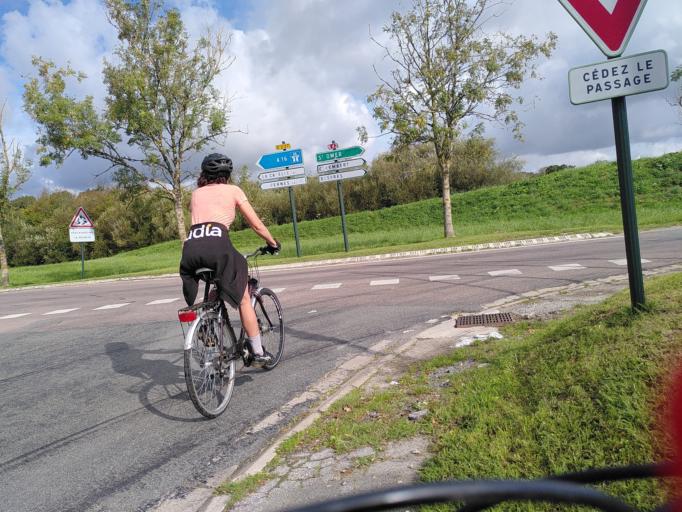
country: FR
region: Nord-Pas-de-Calais
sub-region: Departement du Pas-de-Calais
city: La Capelle-les-Boulogne
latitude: 50.7317
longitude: 1.7160
